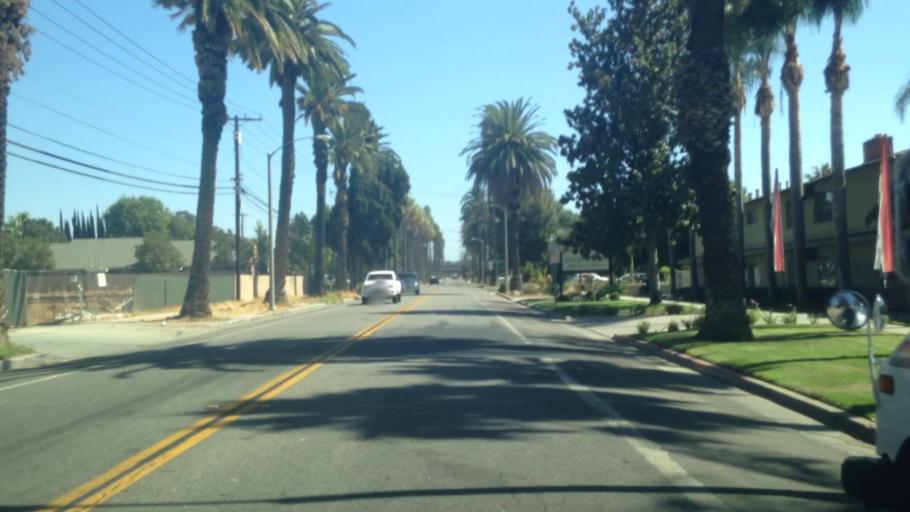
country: US
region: California
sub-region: Riverside County
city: Riverside
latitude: 33.9366
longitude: -117.4163
